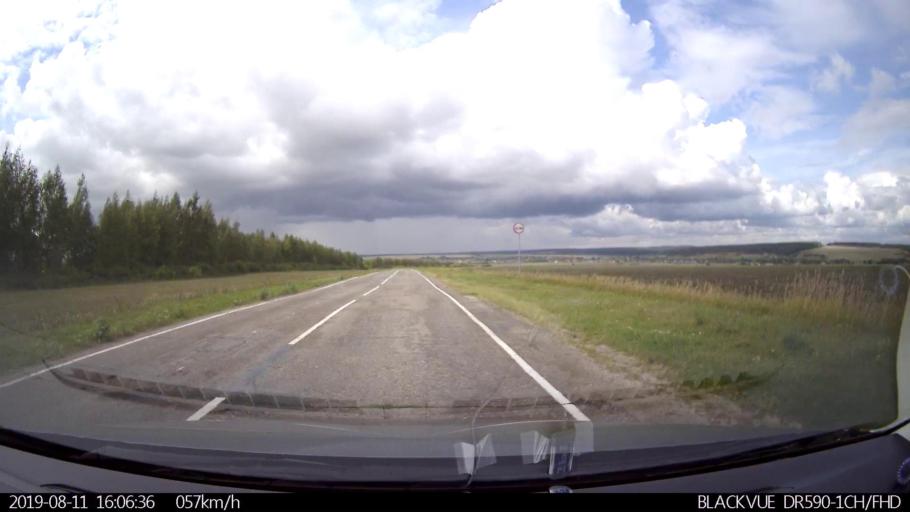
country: RU
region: Ulyanovsk
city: Ignatovka
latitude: 53.9704
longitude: 47.6480
